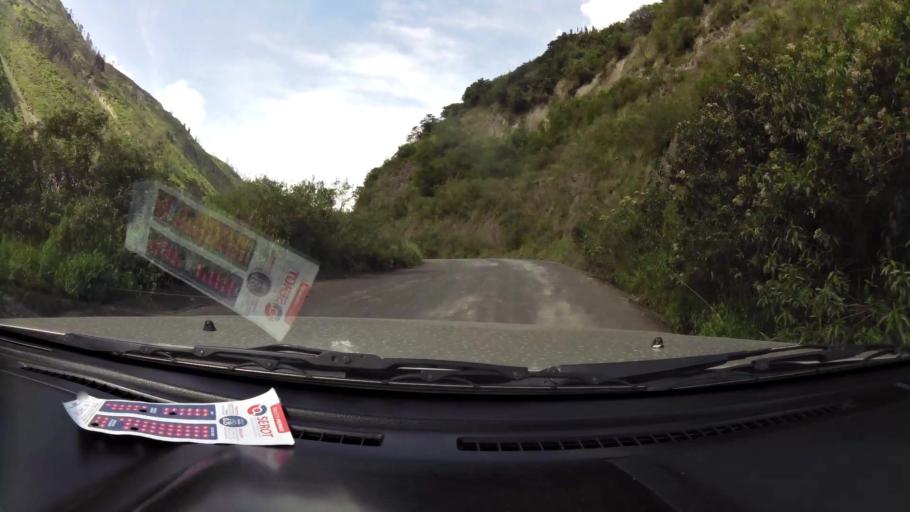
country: EC
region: Tungurahua
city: Banos
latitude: -1.4716
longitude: -78.5123
